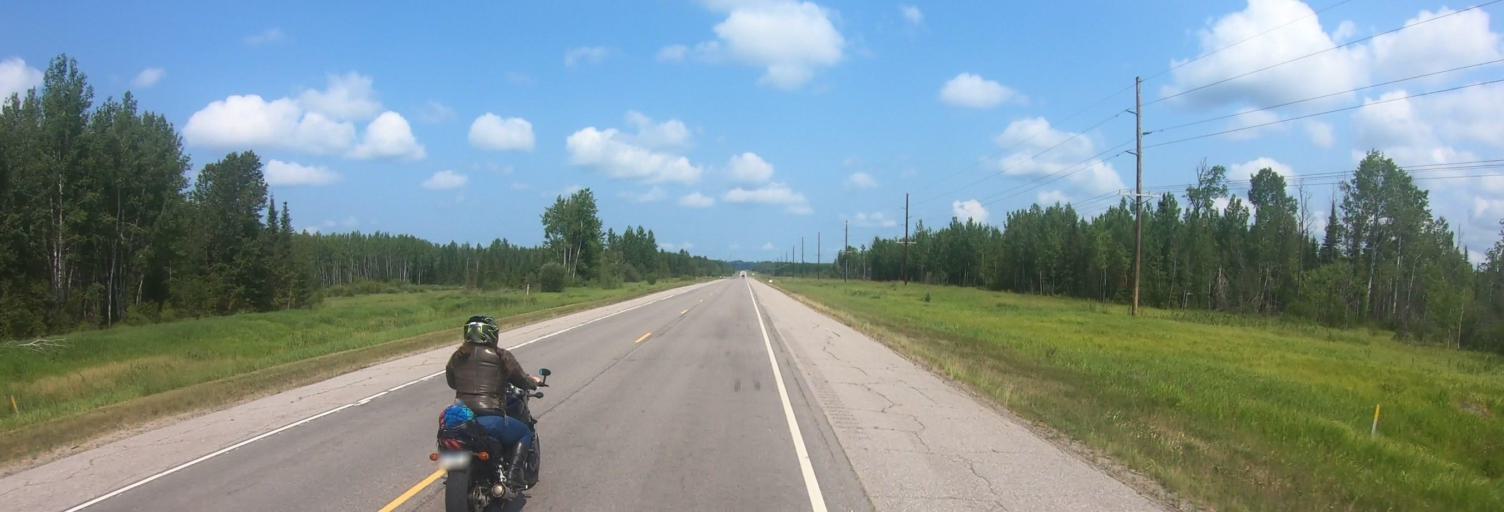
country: US
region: Minnesota
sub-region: Saint Louis County
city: Chisholm
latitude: 47.9361
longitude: -92.8286
